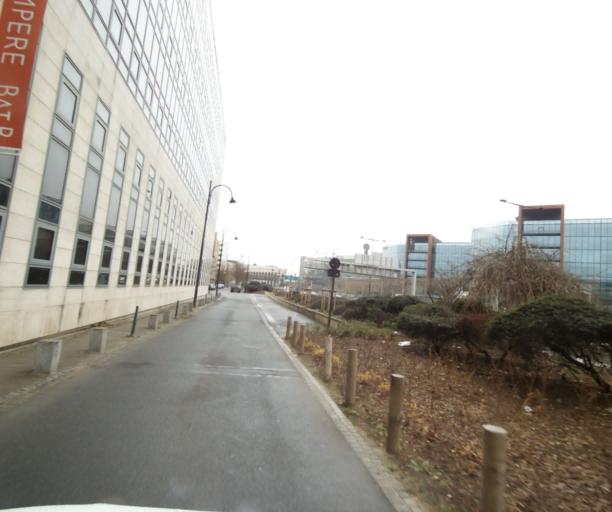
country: FR
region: Ile-de-France
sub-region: Departement des Yvelines
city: Chatou
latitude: 48.8905
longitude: 2.1741
